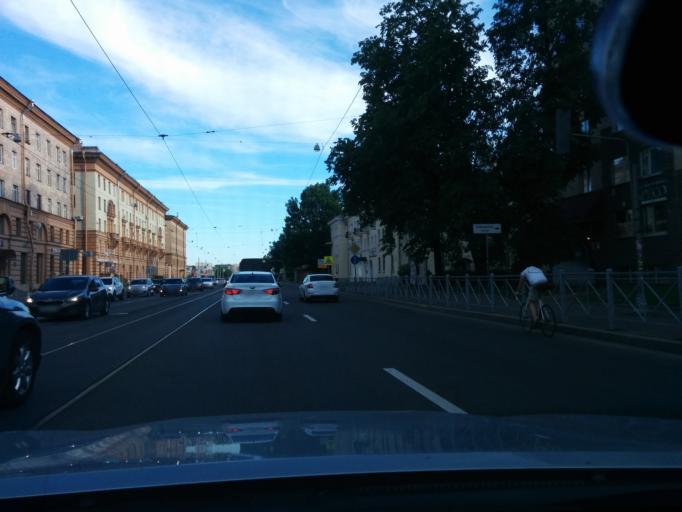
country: RU
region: Leningrad
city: Udel'naya
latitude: 60.0130
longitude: 30.3238
